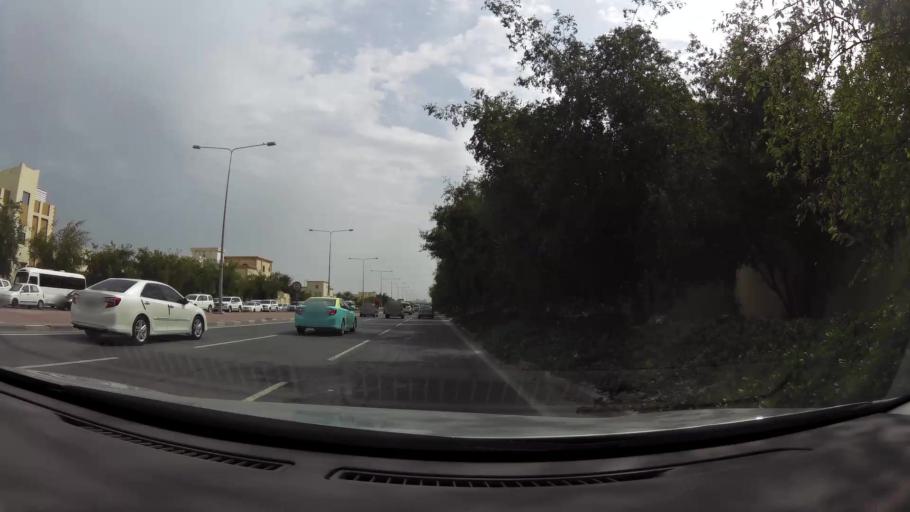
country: QA
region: Baladiyat ad Dawhah
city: Doha
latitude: 25.3419
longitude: 51.5058
